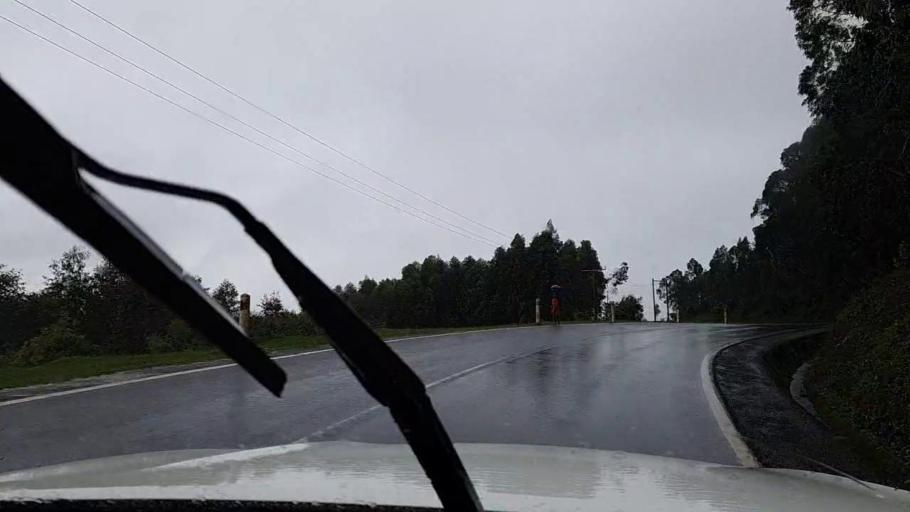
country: RW
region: Western Province
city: Cyangugu
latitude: -2.4627
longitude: 28.9928
